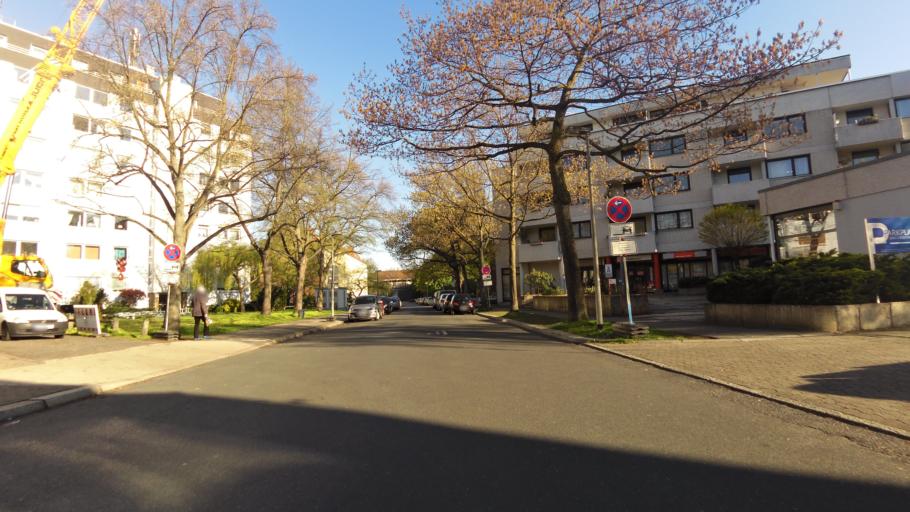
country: DE
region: Lower Saxony
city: Laatzen
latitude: 52.3719
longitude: 9.7922
